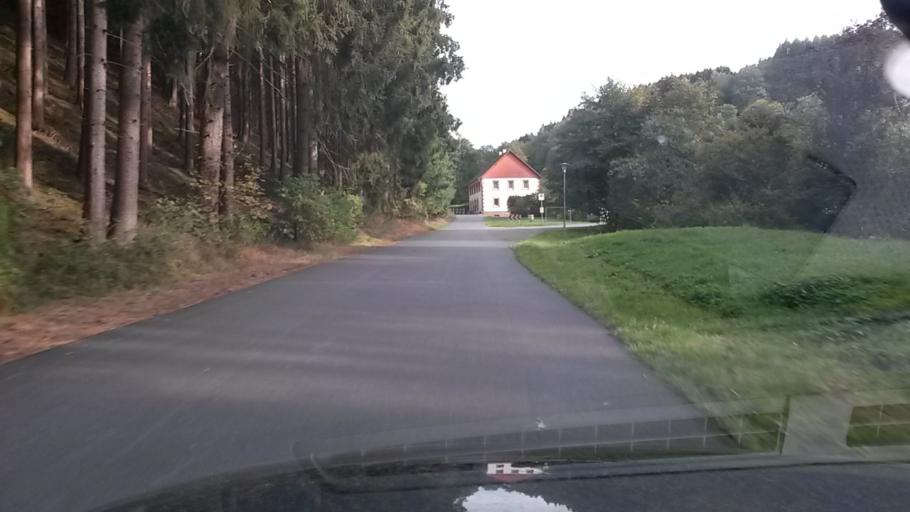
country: DE
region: North Rhine-Westphalia
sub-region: Regierungsbezirk Arnsberg
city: Herscheid
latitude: 51.2190
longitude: 7.7341
